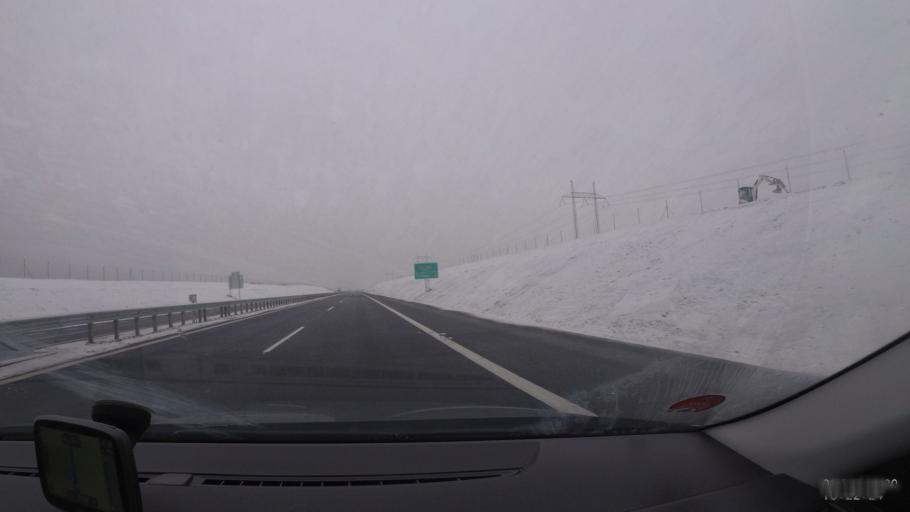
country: CZ
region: Central Bohemia
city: Revnicov
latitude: 50.1774
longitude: 13.8050
